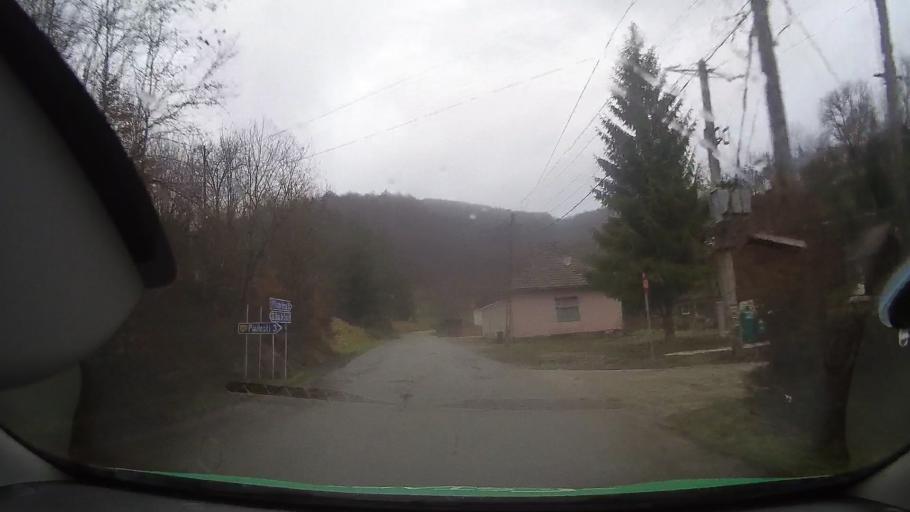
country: RO
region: Alba
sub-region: Comuna Avram Iancu
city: Avram Iancu
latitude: 46.3009
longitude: 22.7613
